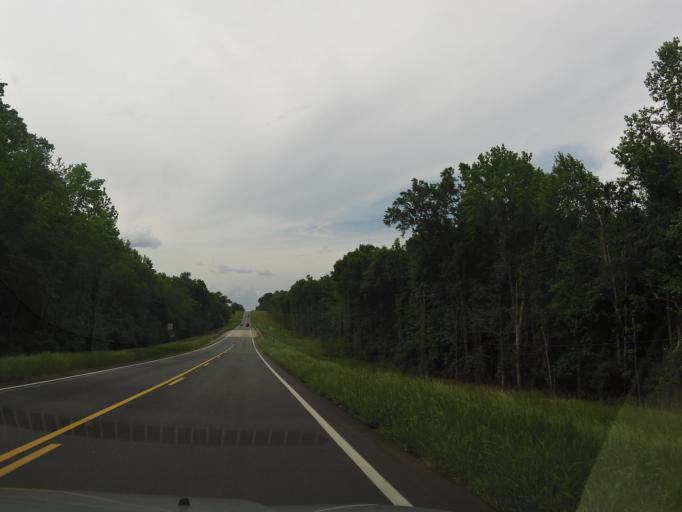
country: US
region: Georgia
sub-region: McDuffie County
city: Thomson
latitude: 33.3387
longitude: -82.4574
